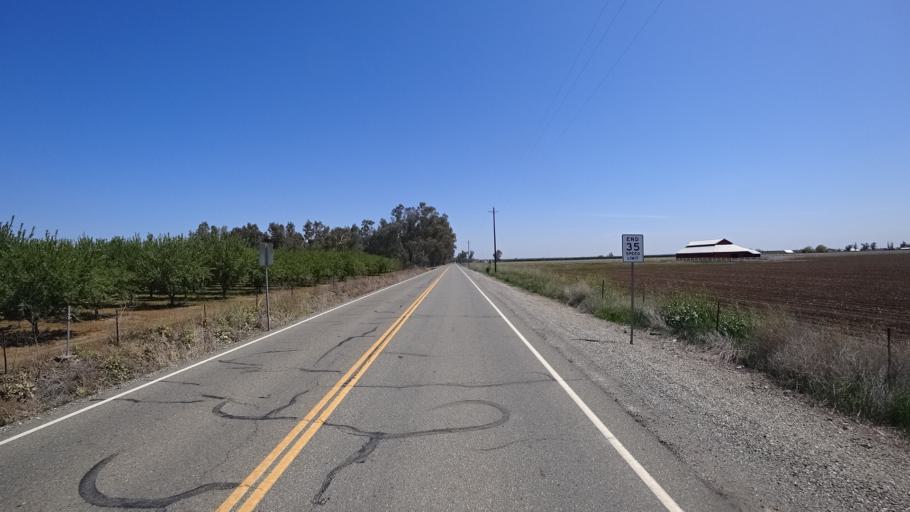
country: US
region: California
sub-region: Glenn County
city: Willows
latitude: 39.5824
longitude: -122.2069
